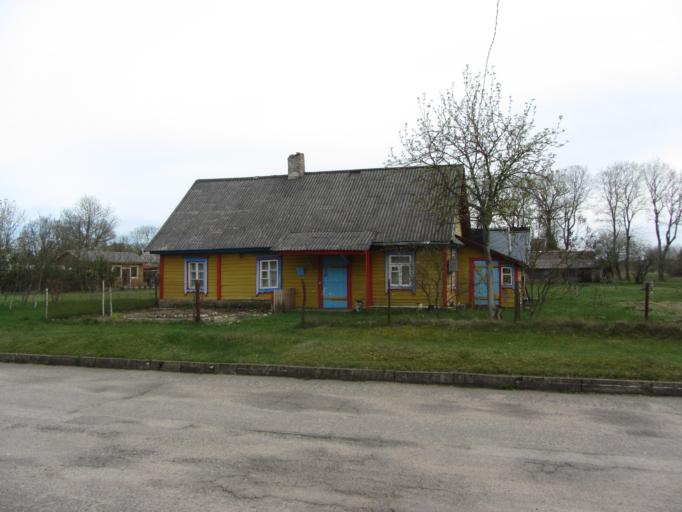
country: LT
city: Zarasai
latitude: 55.5782
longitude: 26.1253
